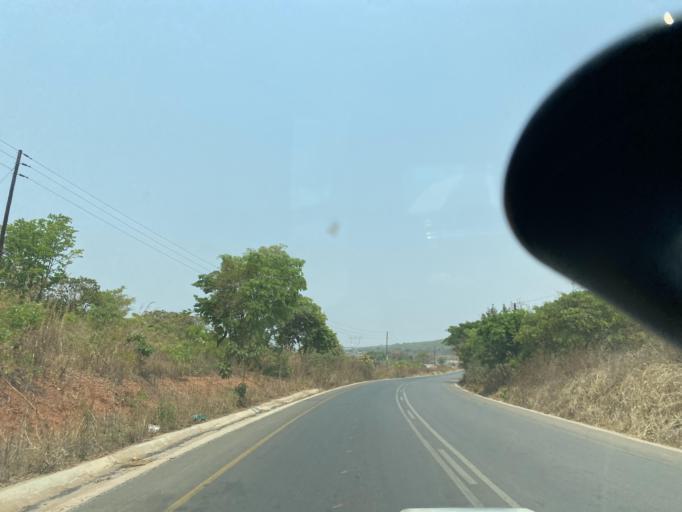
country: ZM
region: Lusaka
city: Lusaka
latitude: -15.5436
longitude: 28.4752
